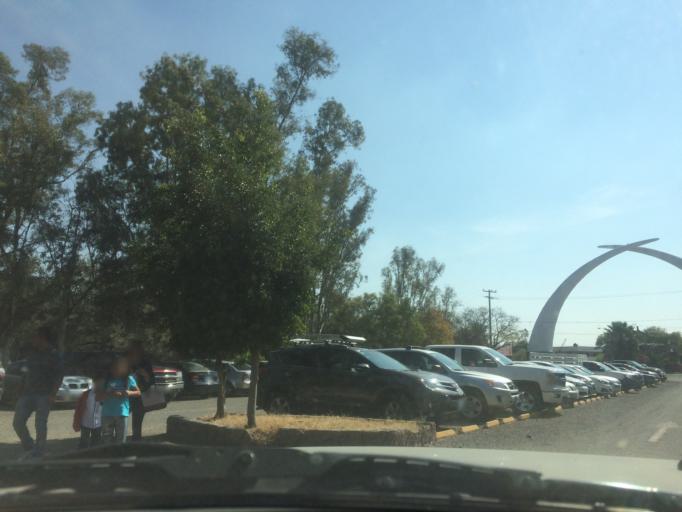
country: MX
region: Guanajuato
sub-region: Leon
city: Medina
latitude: 21.1829
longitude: -101.6505
